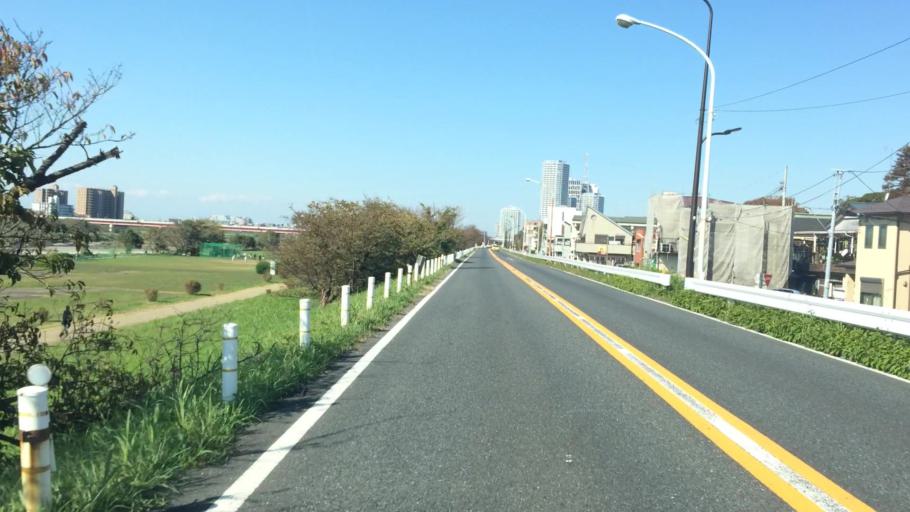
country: JP
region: Tokyo
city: Tokyo
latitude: 35.5998
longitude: 139.6432
